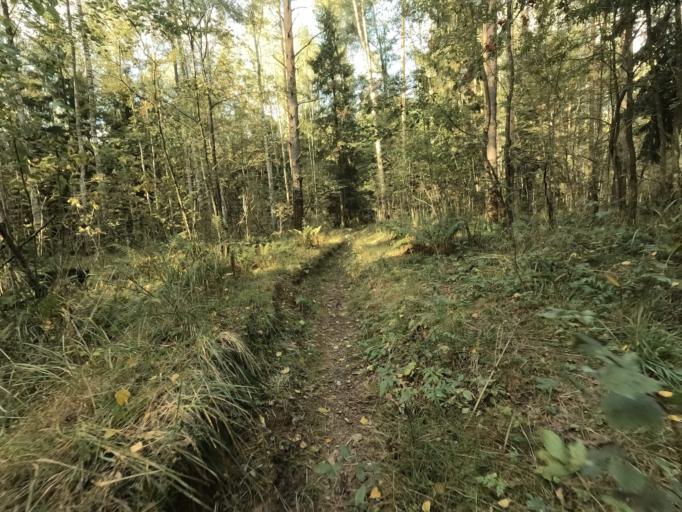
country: RU
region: Leningrad
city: Imeni Sverdlova
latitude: 59.8517
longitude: 30.7286
